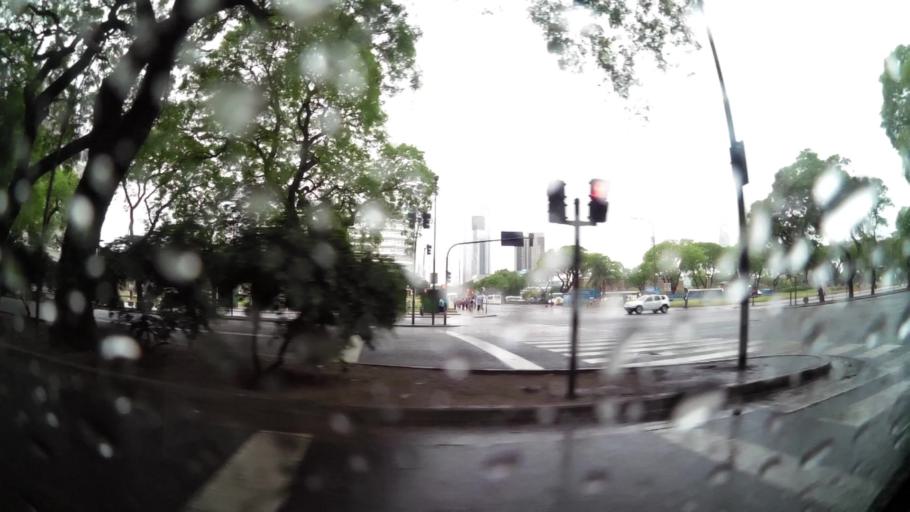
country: AR
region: Buenos Aires F.D.
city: Buenos Aires
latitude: -34.6052
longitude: -58.3702
